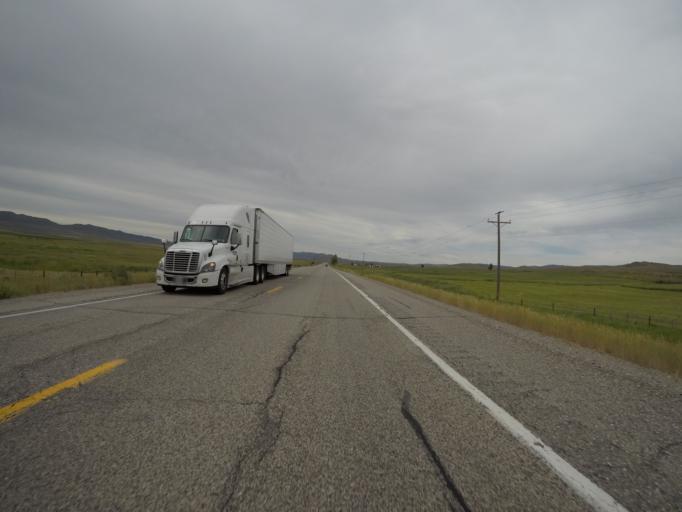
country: US
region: Utah
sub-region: Rich County
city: Randolph
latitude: 42.0002
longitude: -110.9372
